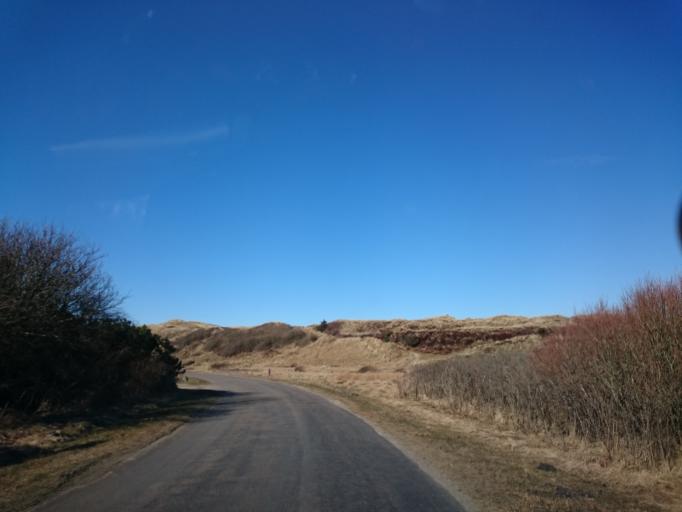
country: DK
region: North Denmark
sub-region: Hjorring Kommune
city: Sindal
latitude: 57.6177
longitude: 10.2809
